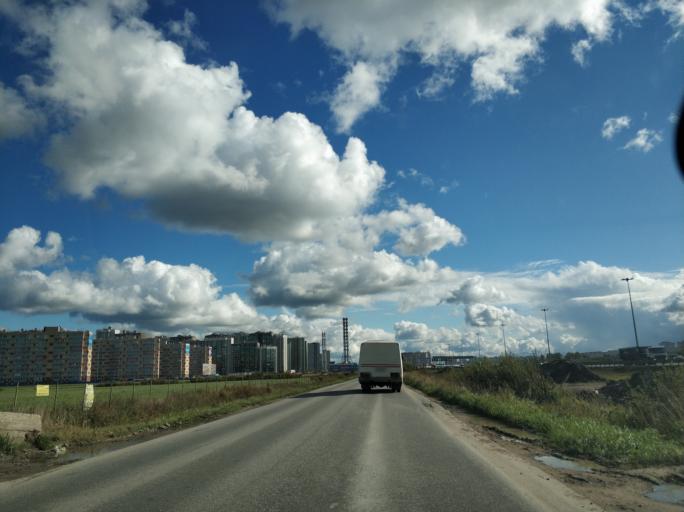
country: RU
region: St.-Petersburg
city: Grazhdanka
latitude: 60.0526
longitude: 30.4061
